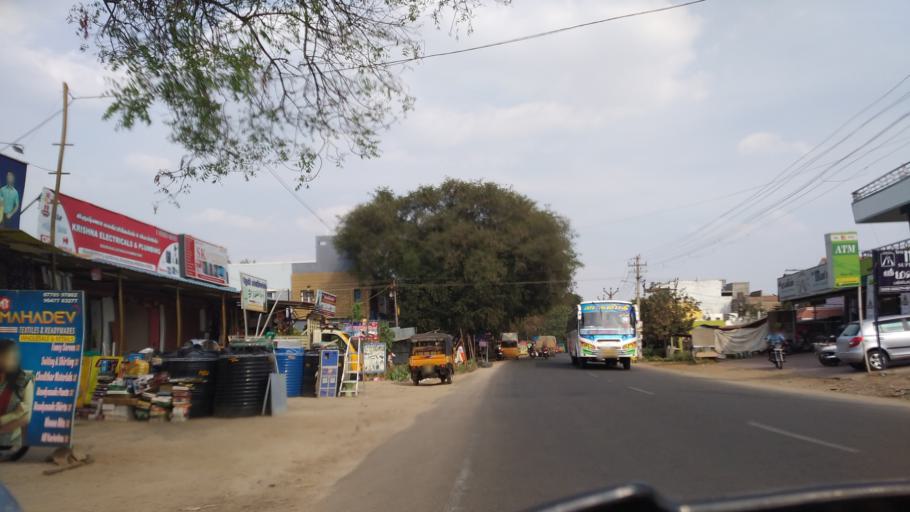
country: IN
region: Tamil Nadu
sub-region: Coimbatore
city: Perur
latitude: 10.9711
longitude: 76.8926
